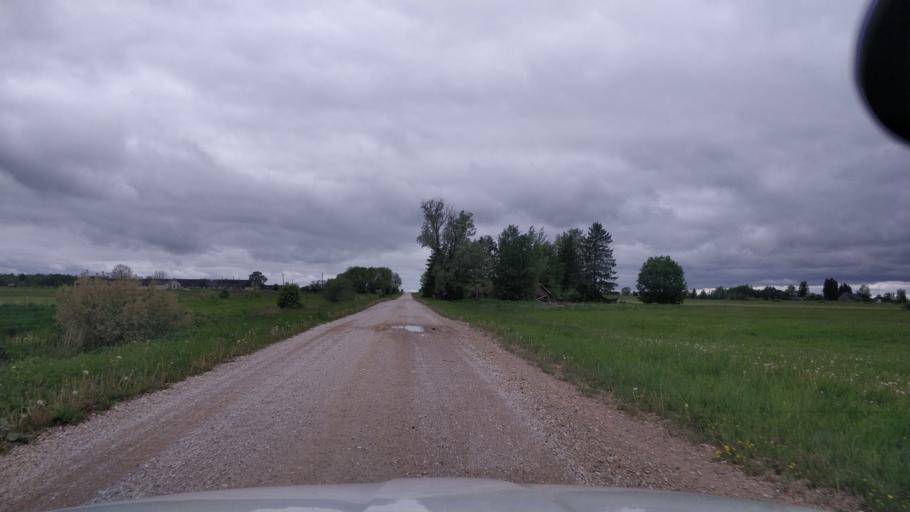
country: EE
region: Raplamaa
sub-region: Maerjamaa vald
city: Marjamaa
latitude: 58.7152
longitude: 24.2581
